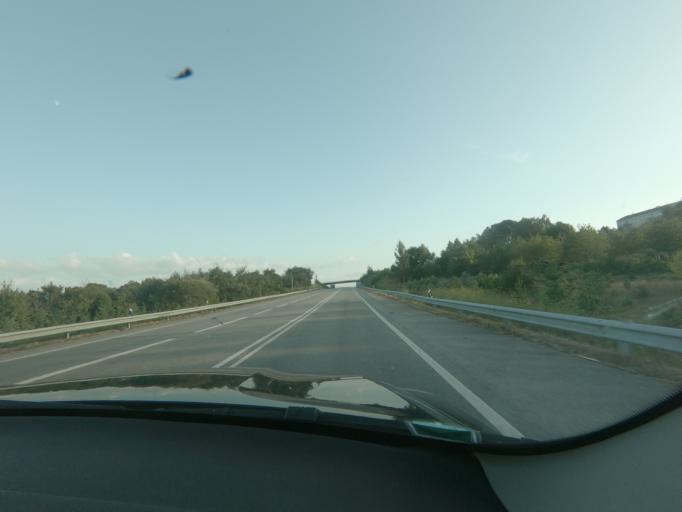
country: PT
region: Viseu
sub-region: Santa Comba Dao
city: Santa Comba Dao
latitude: 40.4118
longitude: -8.1231
